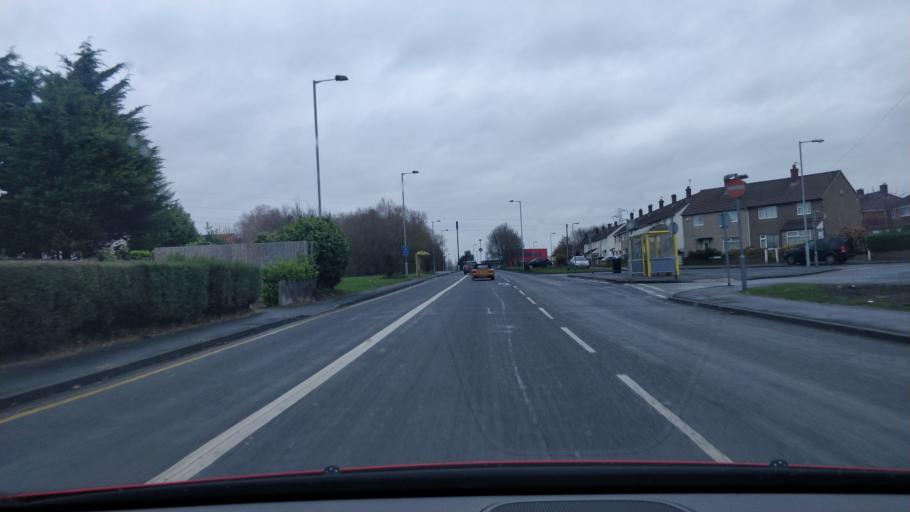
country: GB
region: England
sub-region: Sefton
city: Thornton
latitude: 53.4878
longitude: -2.9915
